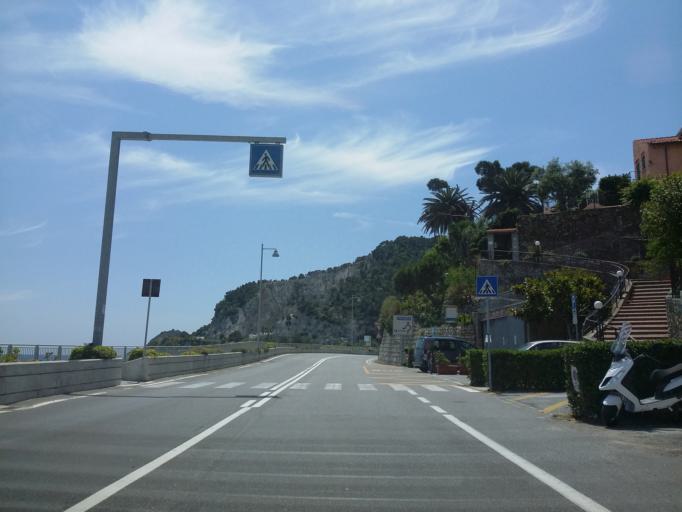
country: IT
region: Liguria
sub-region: Provincia di Savona
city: Bergeggi
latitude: 44.2474
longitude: 8.4453
